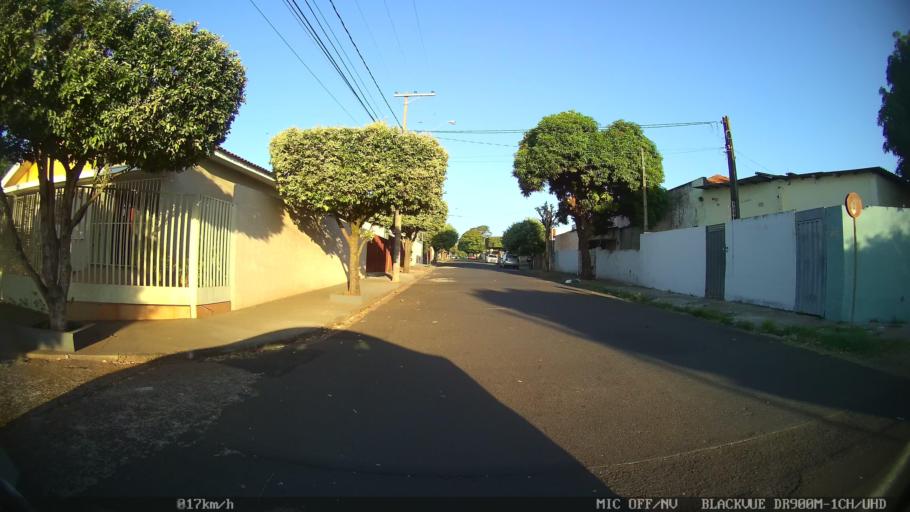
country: BR
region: Sao Paulo
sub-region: Sao Jose Do Rio Preto
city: Sao Jose do Rio Preto
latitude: -20.7954
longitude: -49.3881
